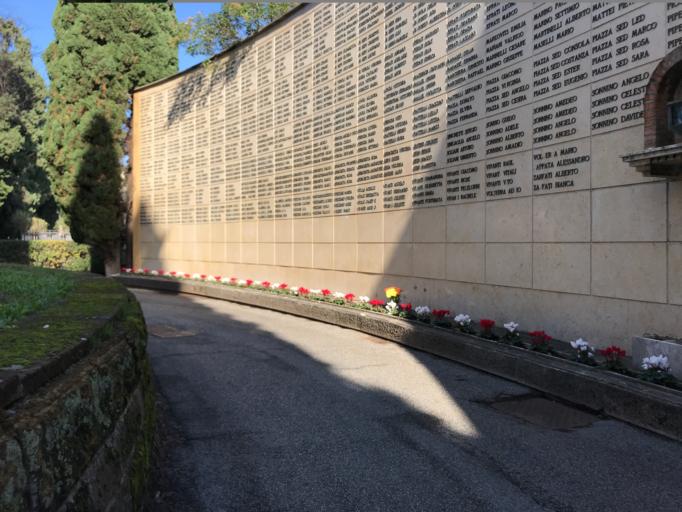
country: IT
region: Latium
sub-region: Citta metropolitana di Roma Capitale
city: Rome
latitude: 41.9004
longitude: 12.5281
